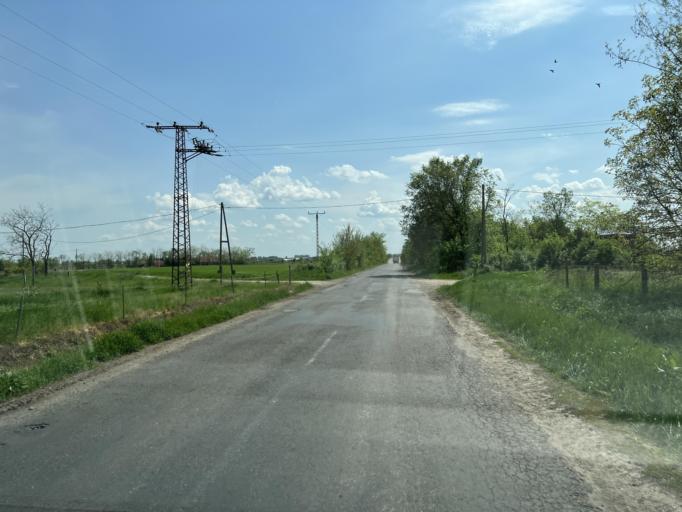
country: HU
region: Pest
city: Cegled
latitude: 47.2073
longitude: 19.7820
